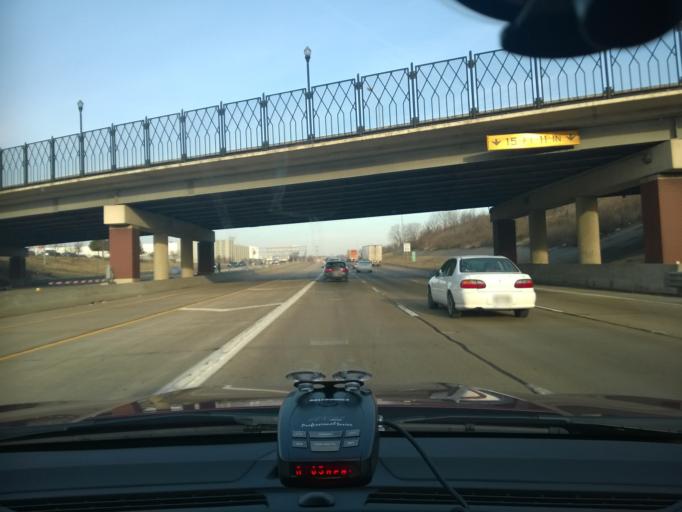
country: US
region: Missouri
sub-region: Saint Louis County
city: Pine Lawn
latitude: 38.6887
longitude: -90.2511
